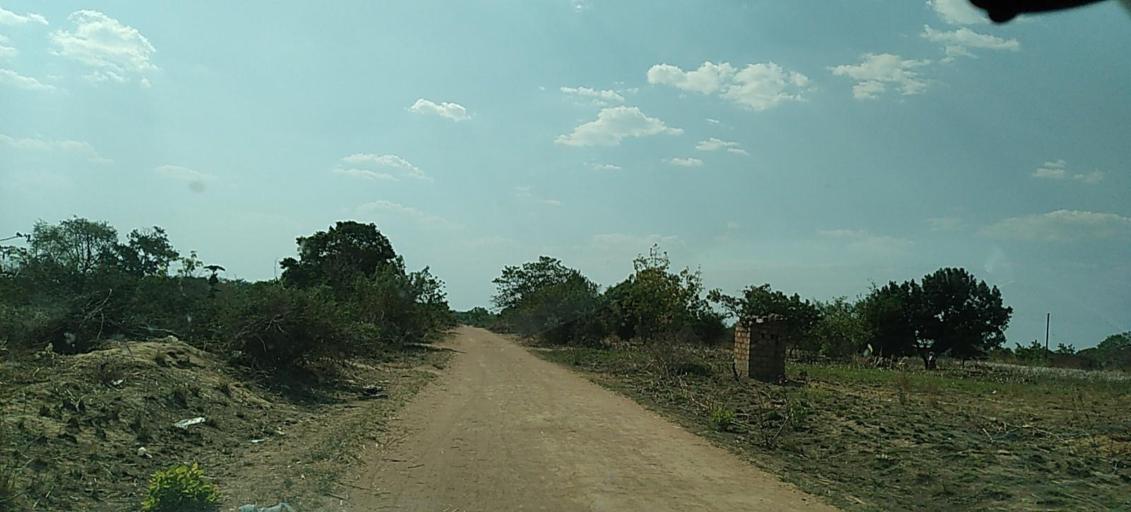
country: ZM
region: North-Western
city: Kalengwa
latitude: -13.1242
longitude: 25.0063
